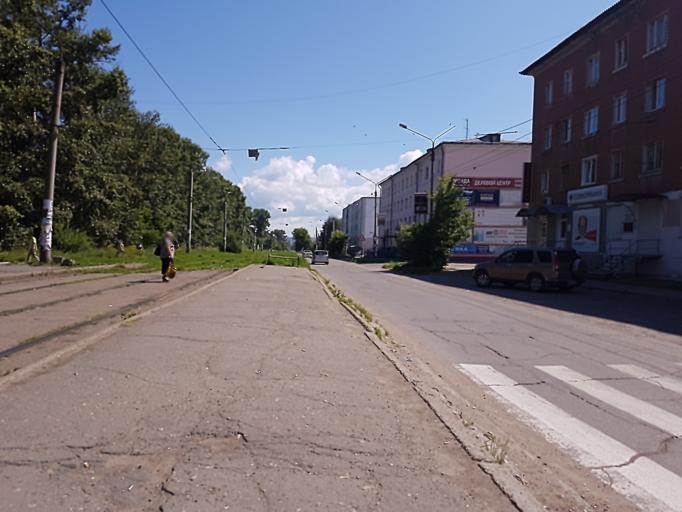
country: RU
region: Irkutsk
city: Usol'ye-Sibirskoye
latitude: 52.7570
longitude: 103.6399
